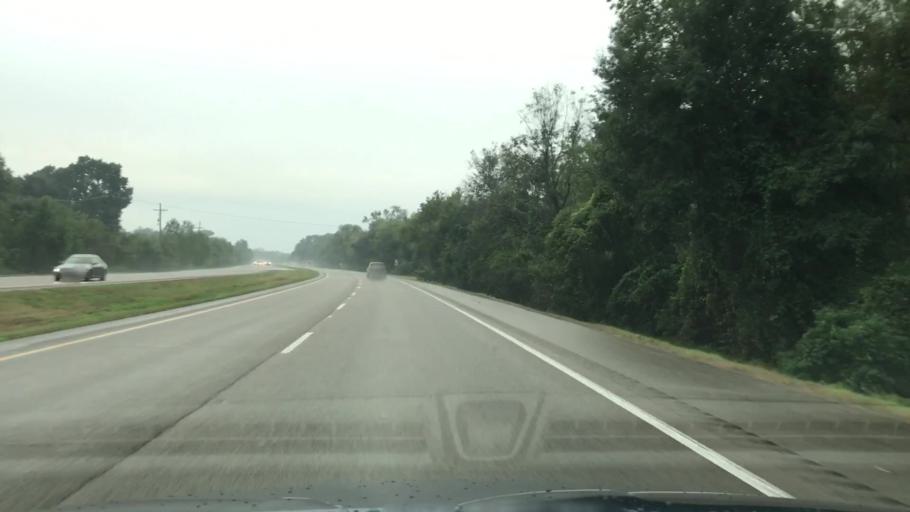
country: US
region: Louisiana
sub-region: Saint Charles Parish
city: Paradis
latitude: 29.8549
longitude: -90.4479
